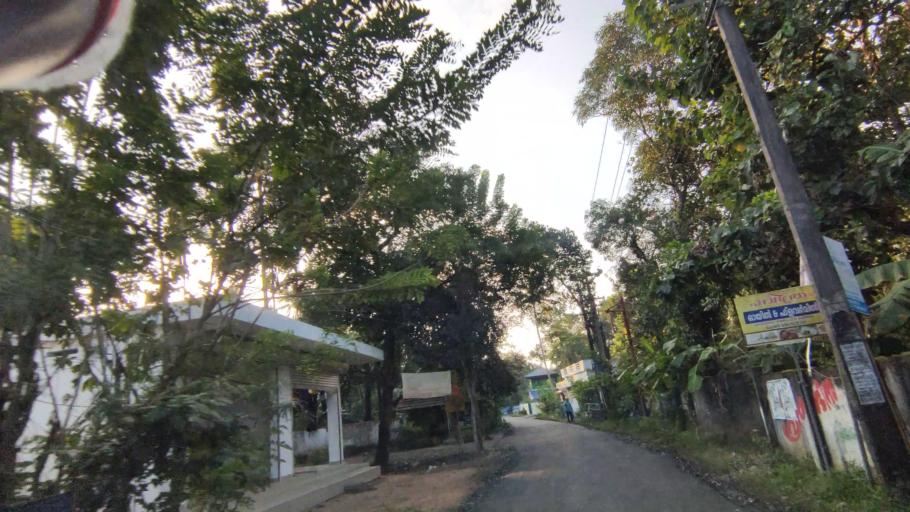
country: IN
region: Kerala
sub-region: Alappuzha
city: Shertallai
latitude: 9.6519
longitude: 76.3510
